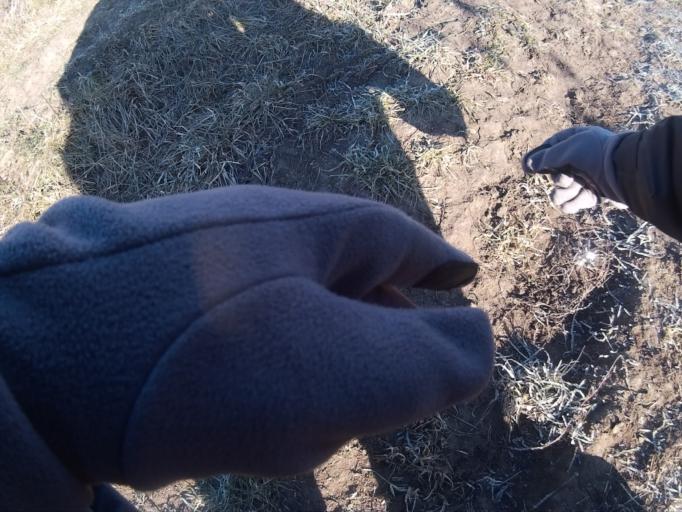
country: HU
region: Borsod-Abauj-Zemplen
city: Putnok
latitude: 48.3837
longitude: 20.4657
